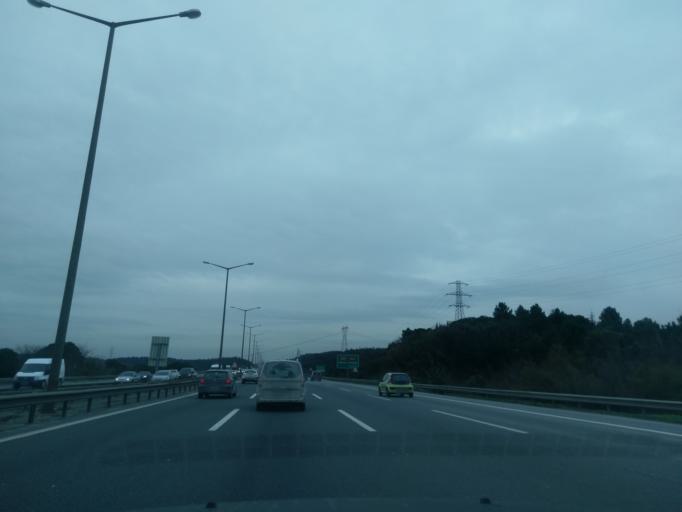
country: TR
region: Istanbul
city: Umraniye
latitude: 41.0777
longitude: 29.0984
